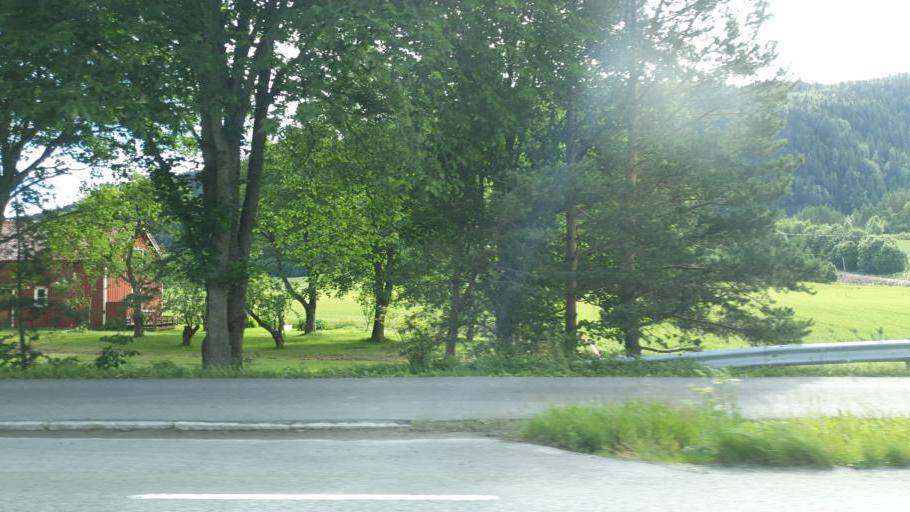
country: NO
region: Sor-Trondelag
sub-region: Melhus
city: Lundamo
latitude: 63.1695
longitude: 10.3142
